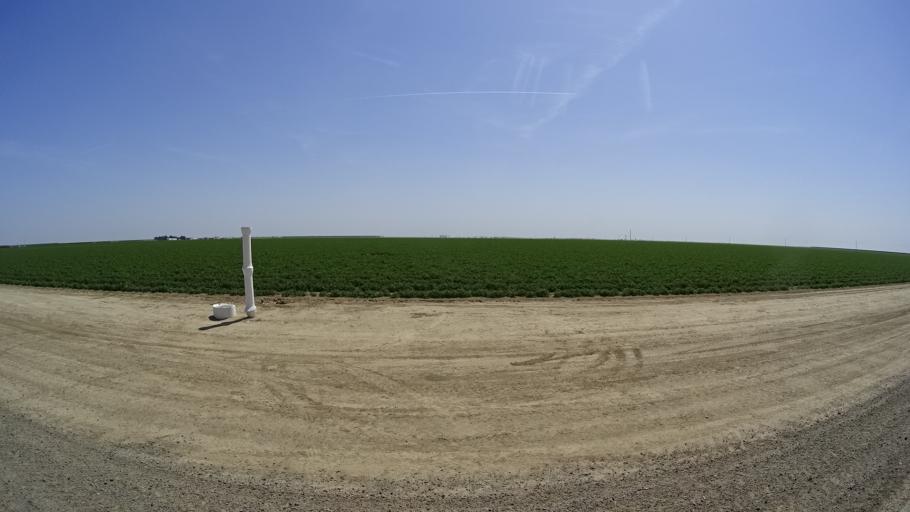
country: US
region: California
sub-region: Fresno County
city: Huron
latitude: 36.1268
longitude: -120.0037
